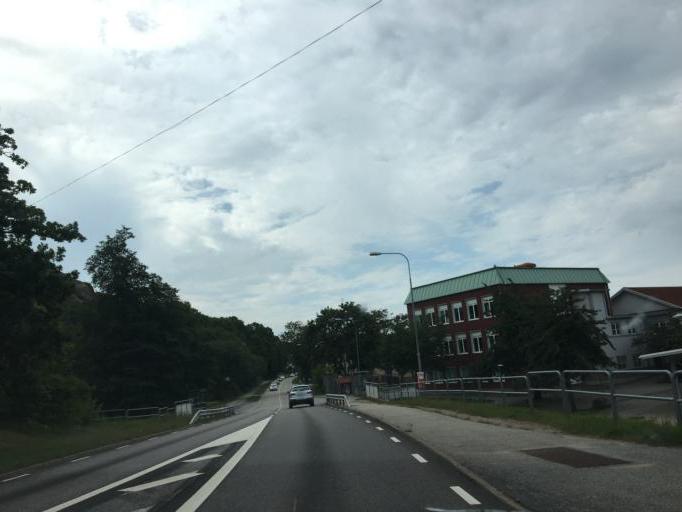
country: SE
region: Vaestra Goetaland
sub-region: Sotenas Kommun
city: Hunnebostrand
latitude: 58.4356
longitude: 11.3002
